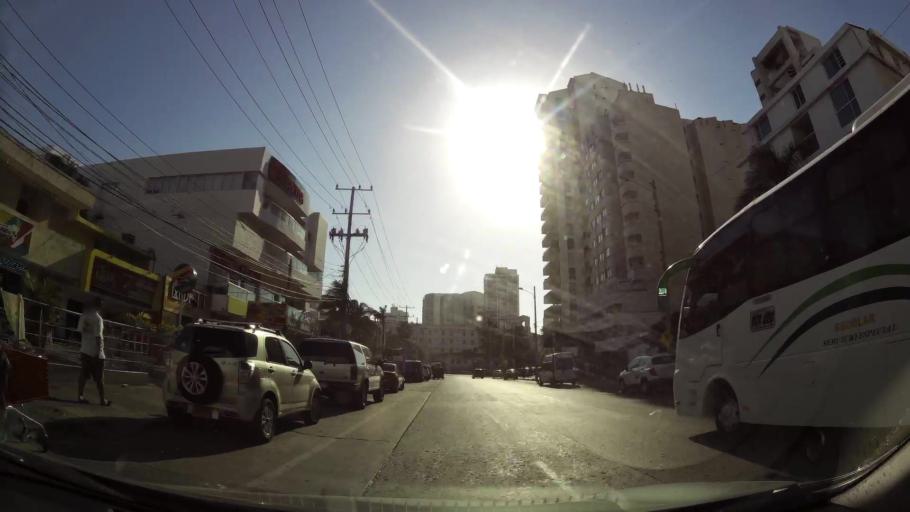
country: CO
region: Bolivar
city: Cartagena
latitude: 10.3992
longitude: -75.5594
